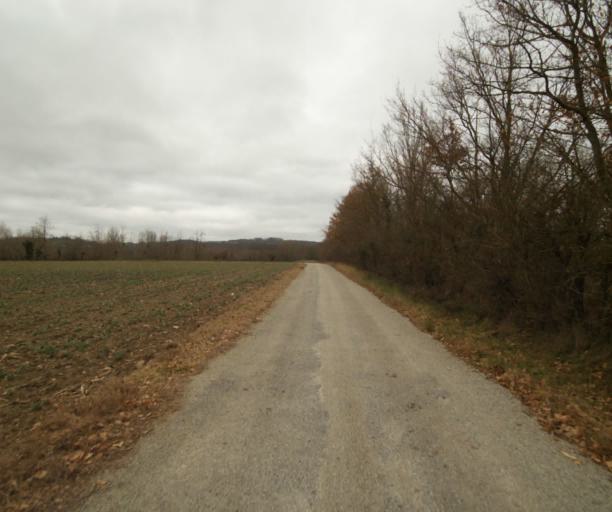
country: FR
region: Midi-Pyrenees
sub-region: Departement de l'Ariege
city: Pamiers
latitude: 43.1478
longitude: 1.5967
